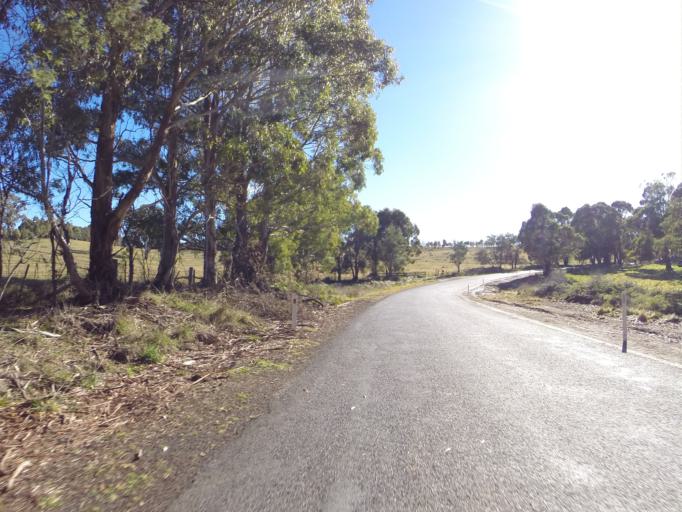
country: AU
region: New South Wales
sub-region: Oberon
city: Oberon
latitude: -33.6273
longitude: 149.8450
